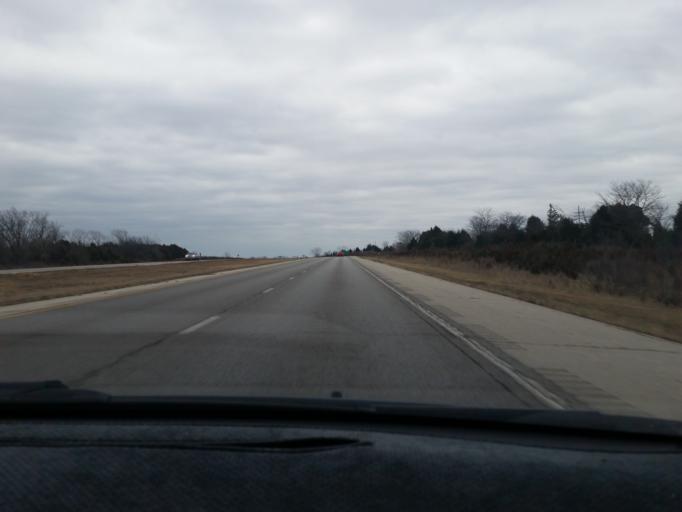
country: US
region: Kansas
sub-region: Douglas County
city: Eudora
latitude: 38.9429
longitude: -95.0495
